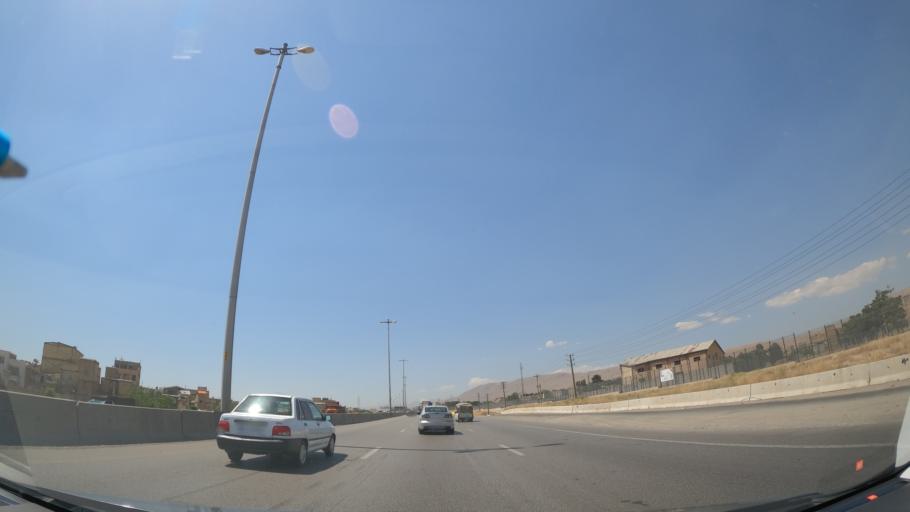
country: IR
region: Alborz
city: Karaj
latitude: 35.8633
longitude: 50.9046
